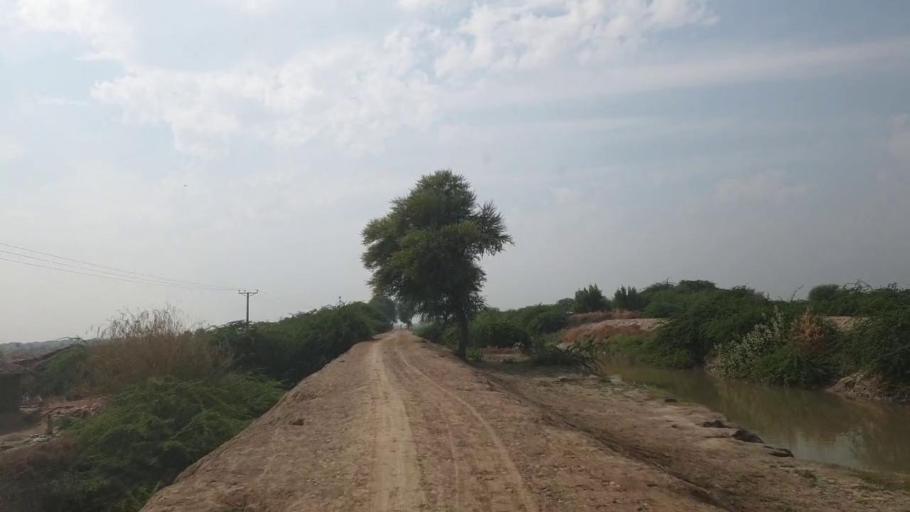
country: PK
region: Sindh
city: Rajo Khanani
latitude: 24.9663
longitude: 69.0018
